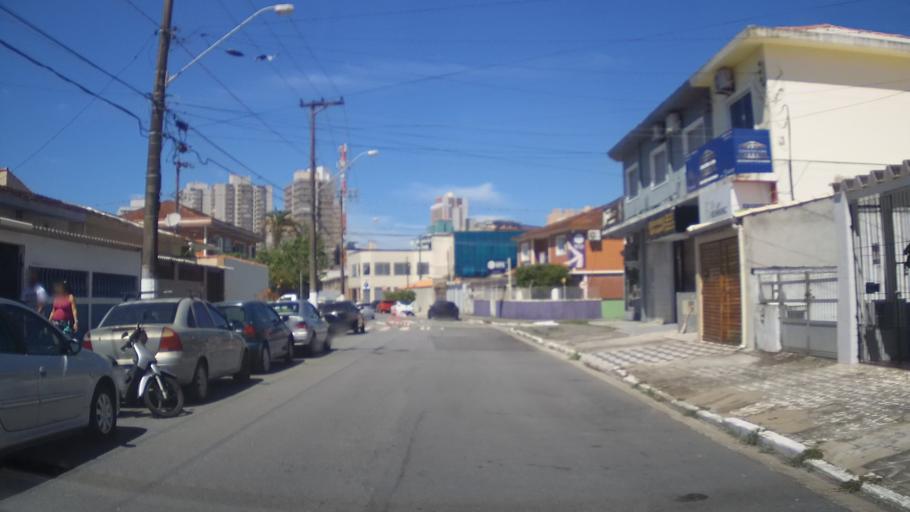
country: BR
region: Sao Paulo
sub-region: Praia Grande
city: Praia Grande
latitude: -24.0057
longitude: -46.4166
